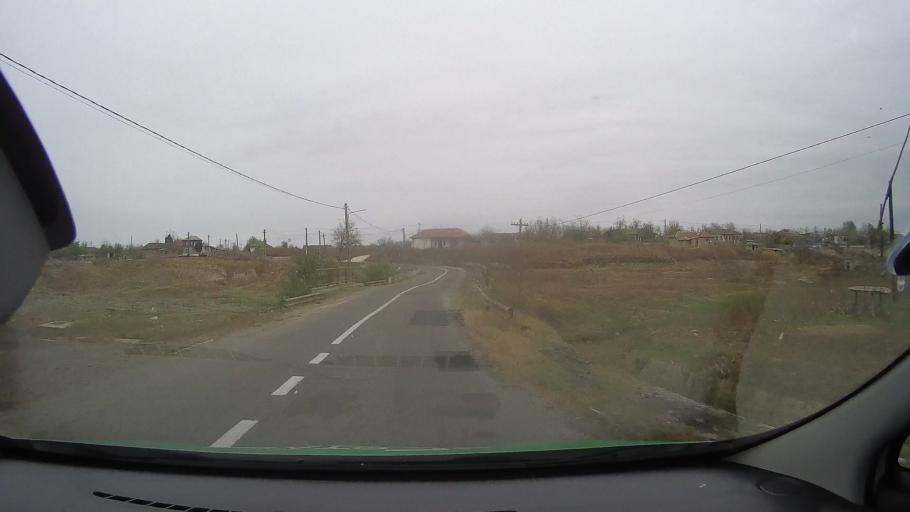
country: RO
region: Constanta
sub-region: Comuna Vulturu
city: Vulturu
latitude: 44.7002
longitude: 28.2404
